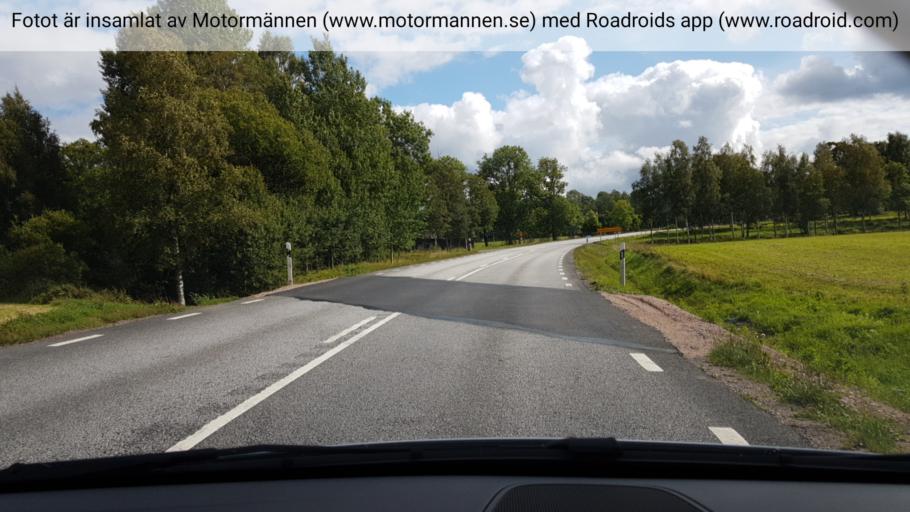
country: SE
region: Joenkoeping
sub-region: Mullsjo Kommun
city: Mullsjoe
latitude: 58.0358
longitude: 13.8361
